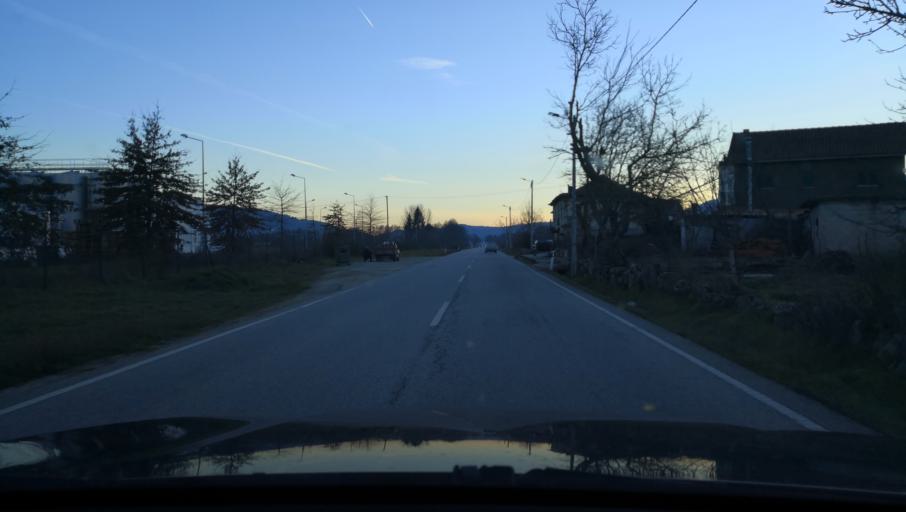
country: PT
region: Vila Real
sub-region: Vila Pouca de Aguiar
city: Vila Pouca de Aguiar
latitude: 41.4472
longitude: -7.6716
